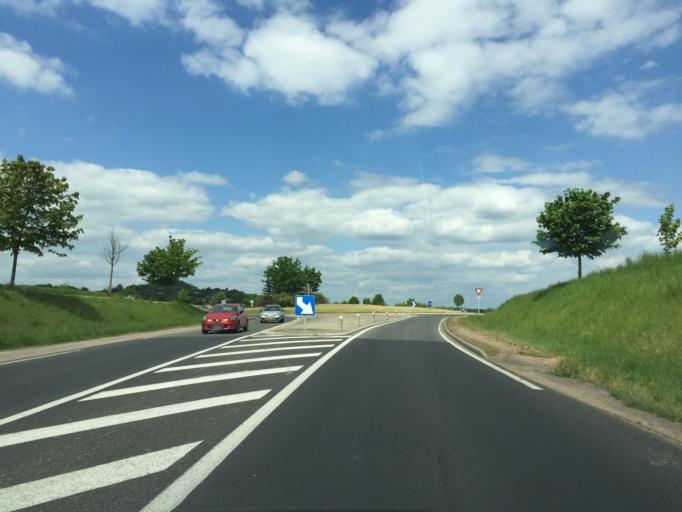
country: FR
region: Auvergne
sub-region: Departement du Puy-de-Dome
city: Aigueperse
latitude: 46.0223
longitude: 3.2166
